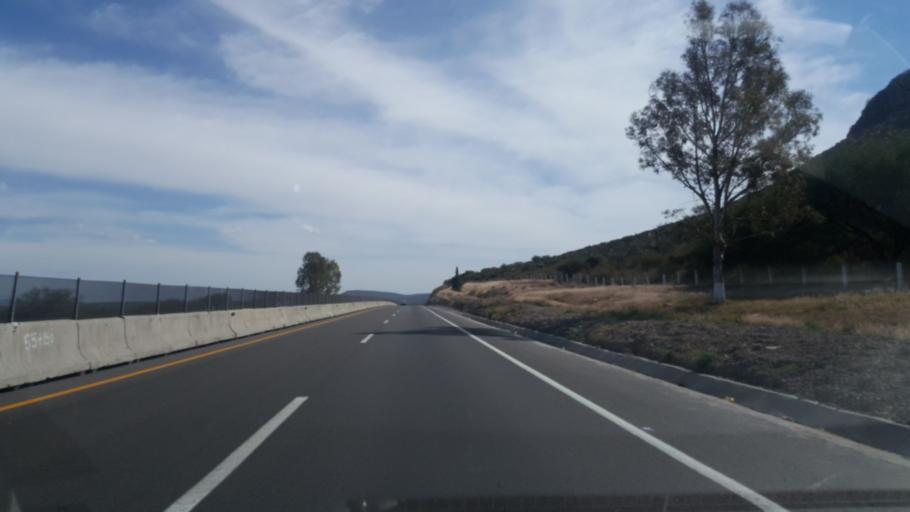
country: MX
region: Jalisco
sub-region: Lagos de Moreno
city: Cristeros [Fraccionamiento]
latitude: 21.2917
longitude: -102.0083
